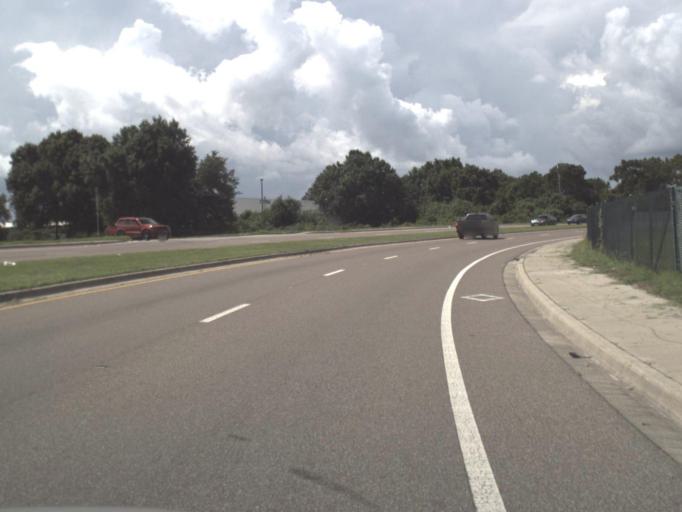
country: US
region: Florida
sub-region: Hillsborough County
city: Egypt Lake-Leto
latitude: 28.0094
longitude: -82.5317
